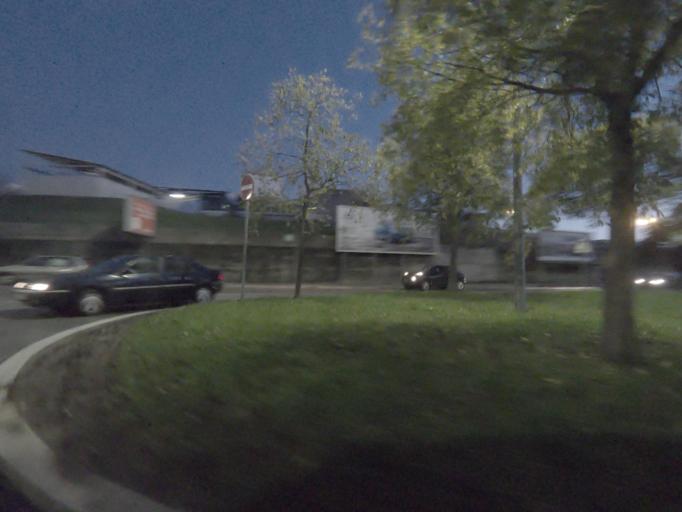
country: PT
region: Porto
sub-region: Matosinhos
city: Senhora da Hora
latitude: 41.1705
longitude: -8.6425
